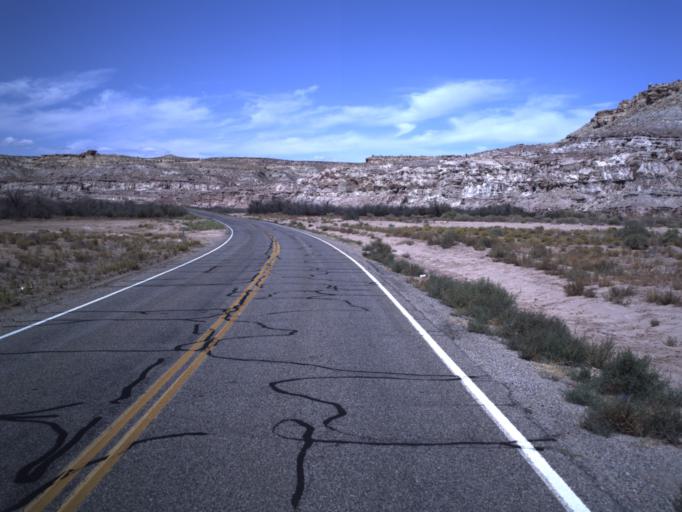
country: US
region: Utah
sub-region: San Juan County
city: Blanding
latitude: 37.2538
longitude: -109.2586
